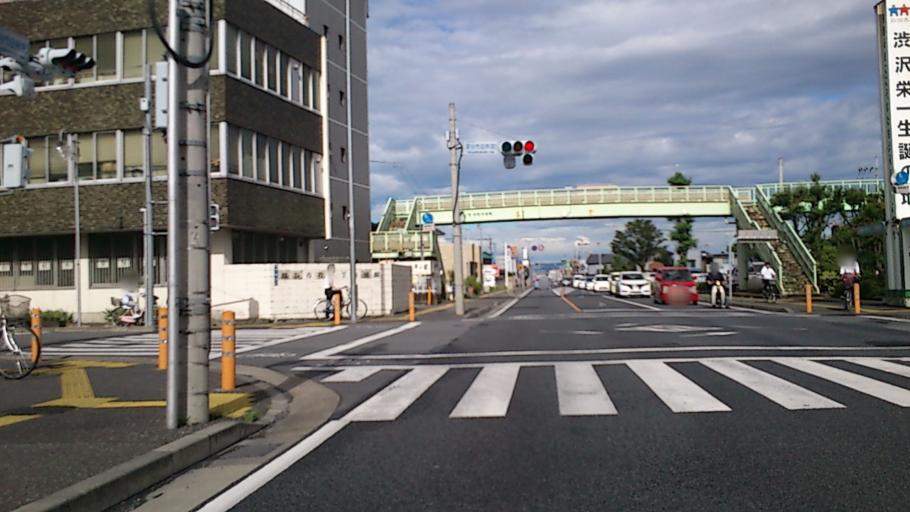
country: JP
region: Saitama
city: Fukayacho
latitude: 36.1968
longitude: 139.2829
